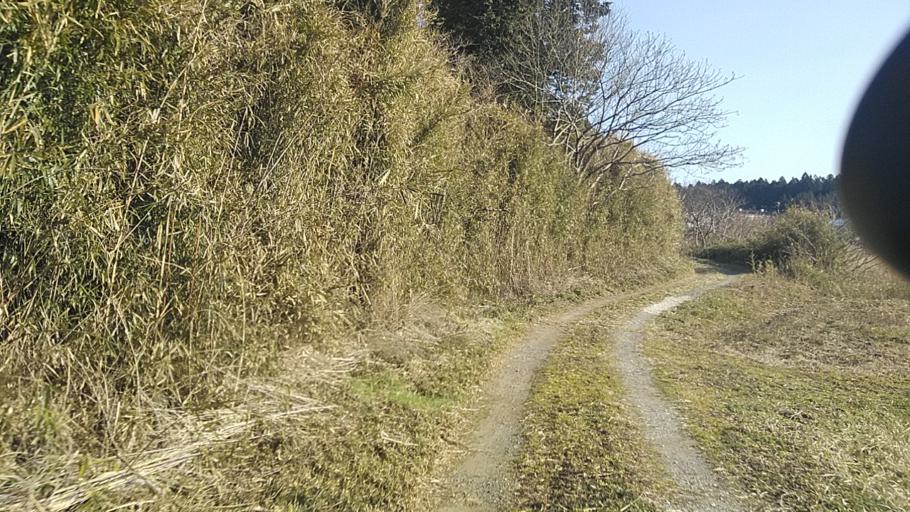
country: JP
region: Chiba
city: Sawara
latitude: 35.8182
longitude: 140.5144
